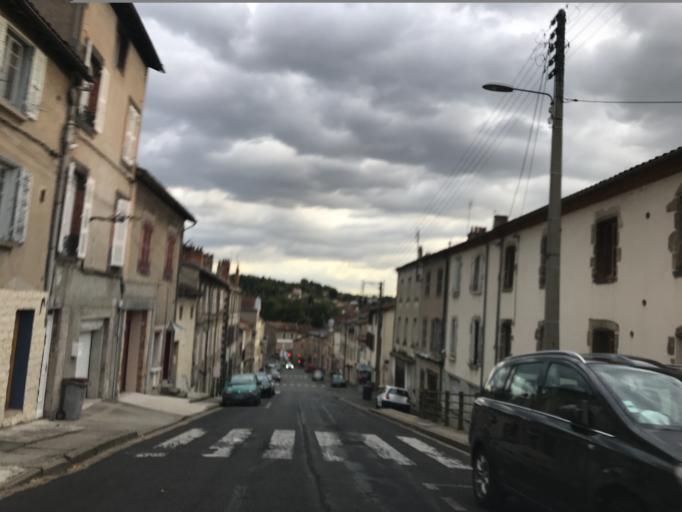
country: FR
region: Auvergne
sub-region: Departement du Puy-de-Dome
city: Thiers
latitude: 45.8539
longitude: 3.5423
